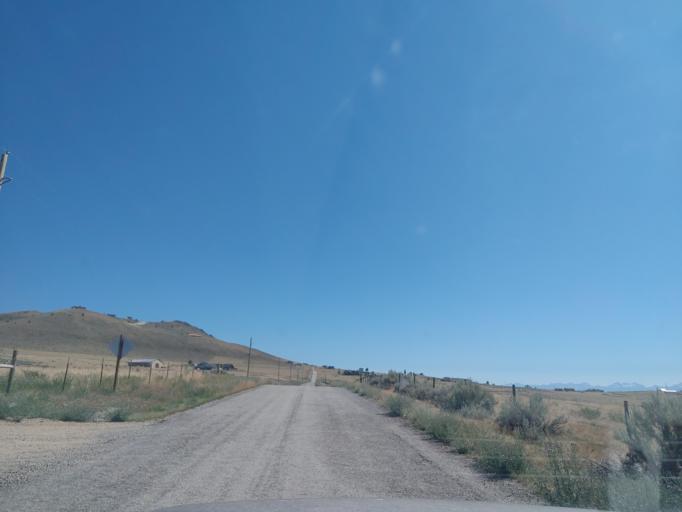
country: US
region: Montana
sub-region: Ravalli County
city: Stevensville
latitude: 46.3587
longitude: -114.0378
